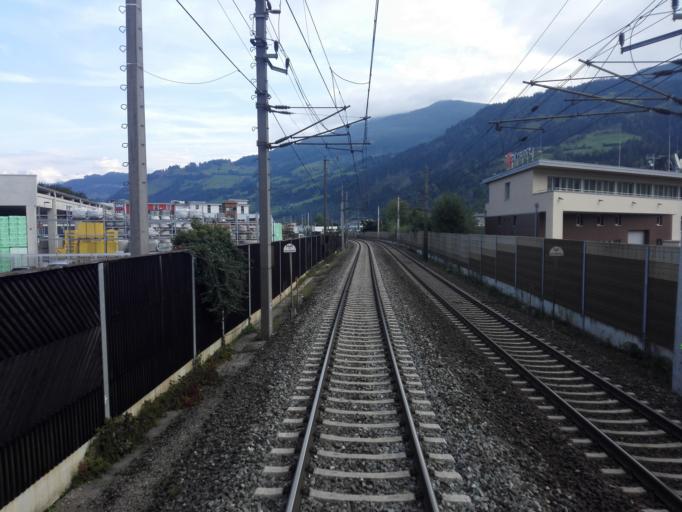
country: AT
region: Salzburg
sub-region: Politischer Bezirk Sankt Johann im Pongau
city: Sankt Johann im Pongau
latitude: 47.3550
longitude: 13.1983
